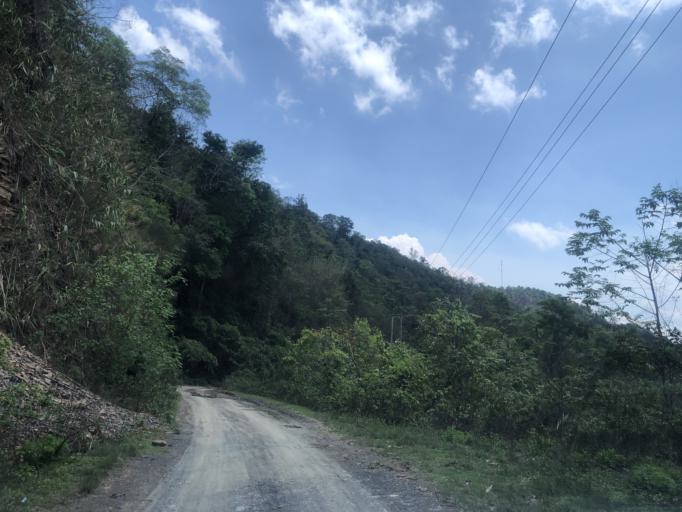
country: LA
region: Phongsali
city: Phongsali
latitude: 21.4465
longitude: 102.1635
